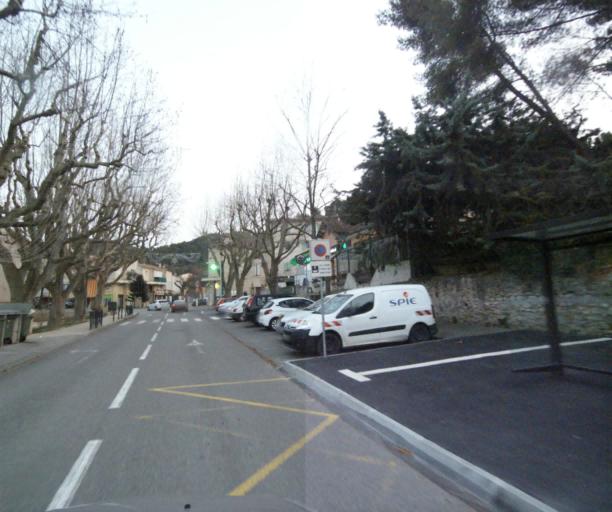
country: FR
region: Provence-Alpes-Cote d'Azur
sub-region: Departement des Bouches-du-Rhone
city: Simiane-Collongue
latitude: 43.4295
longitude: 5.4359
